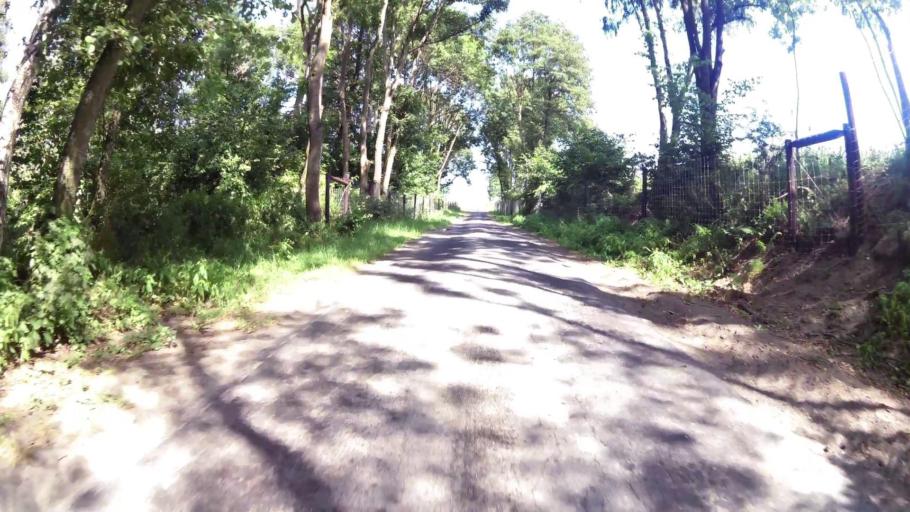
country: PL
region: West Pomeranian Voivodeship
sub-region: Powiat choszczenski
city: Choszczno
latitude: 53.2532
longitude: 15.4254
